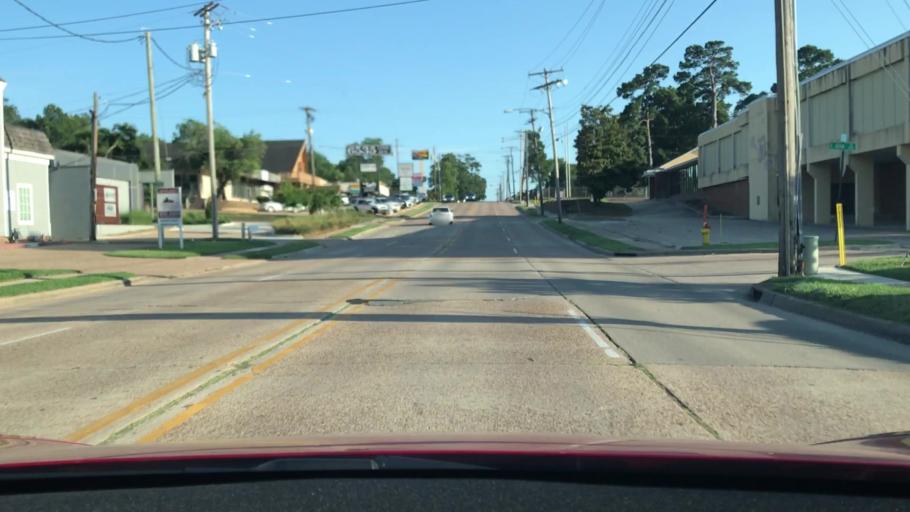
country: US
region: Louisiana
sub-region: Bossier Parish
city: Bossier City
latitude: 32.4473
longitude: -93.7460
